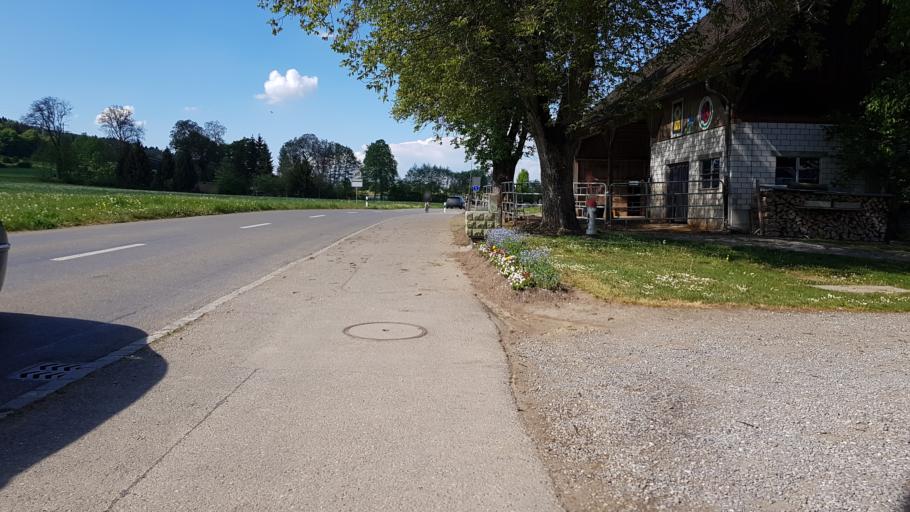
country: CH
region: Lucerne
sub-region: Hochdorf District
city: Hitzkirch
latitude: 47.2121
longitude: 8.2421
